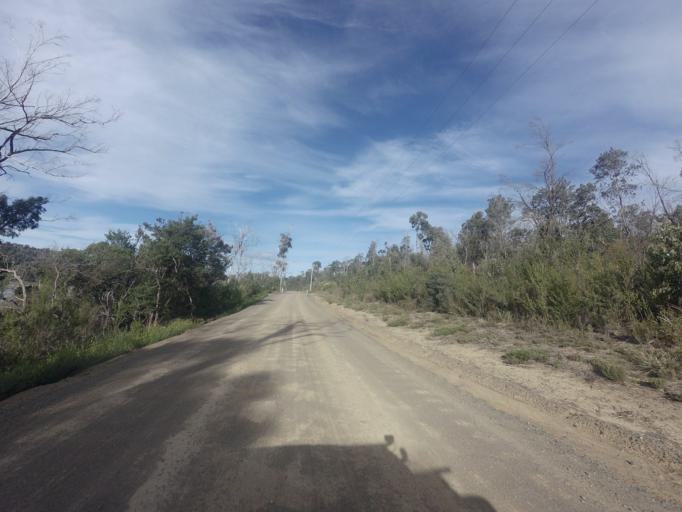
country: AU
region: Tasmania
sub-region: Sorell
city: Sorell
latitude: -42.9582
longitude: 147.8461
